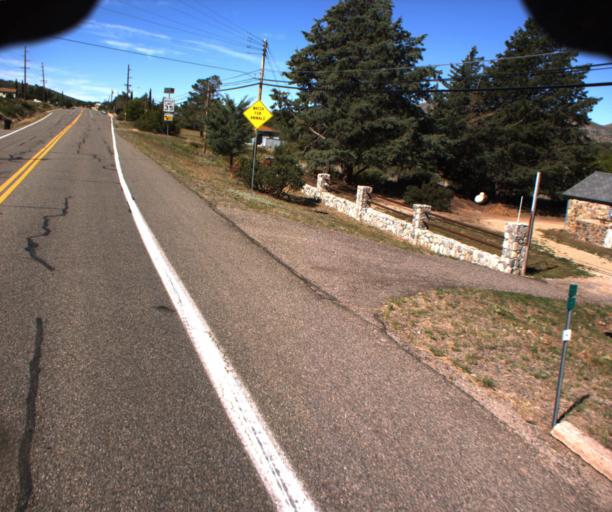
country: US
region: Arizona
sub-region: Yavapai County
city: Congress
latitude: 34.2282
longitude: -112.7416
